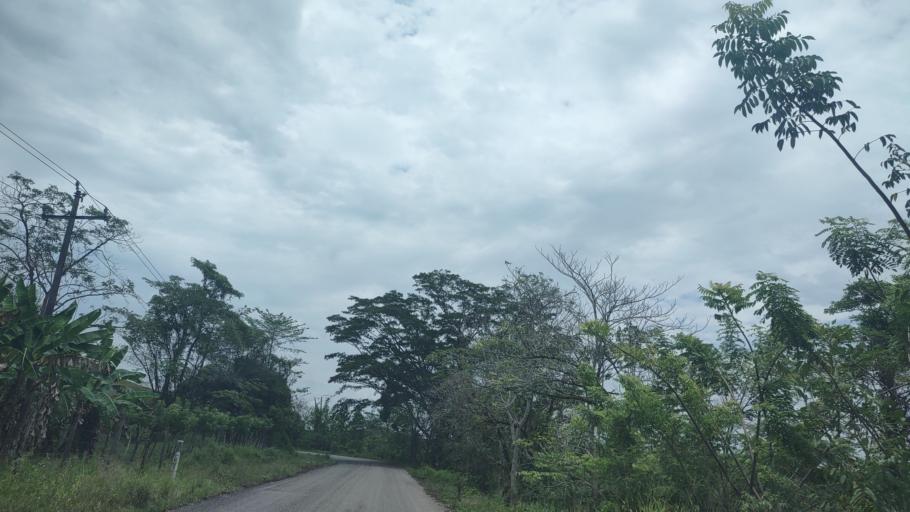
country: MX
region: Tabasco
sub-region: Huimanguillo
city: Francisco Rueda
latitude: 17.5382
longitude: -94.1261
